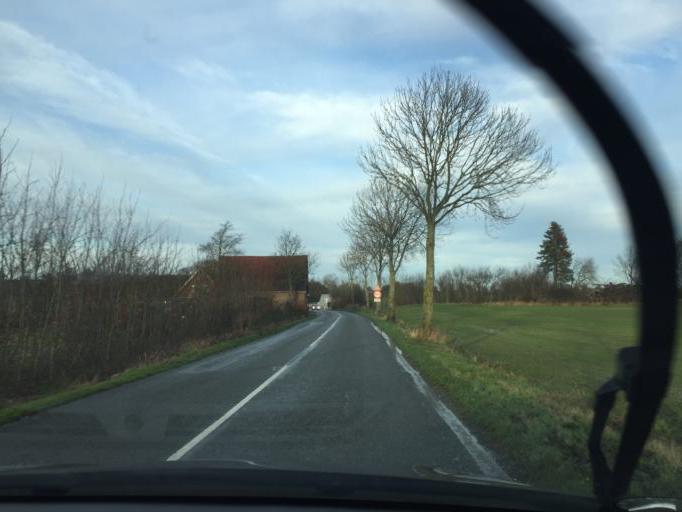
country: DK
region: South Denmark
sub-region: Faaborg-Midtfyn Kommune
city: Ringe
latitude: 55.1805
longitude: 10.4066
